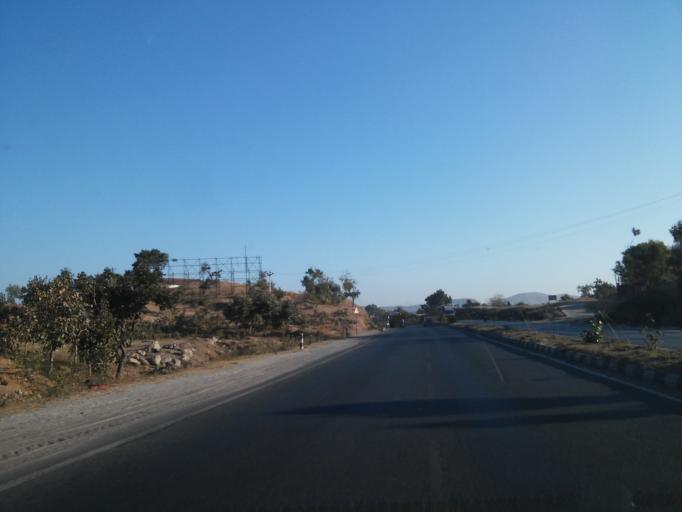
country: IN
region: Rajasthan
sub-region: Dungarpur
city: Dungarpur
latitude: 23.9377
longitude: 73.5725
